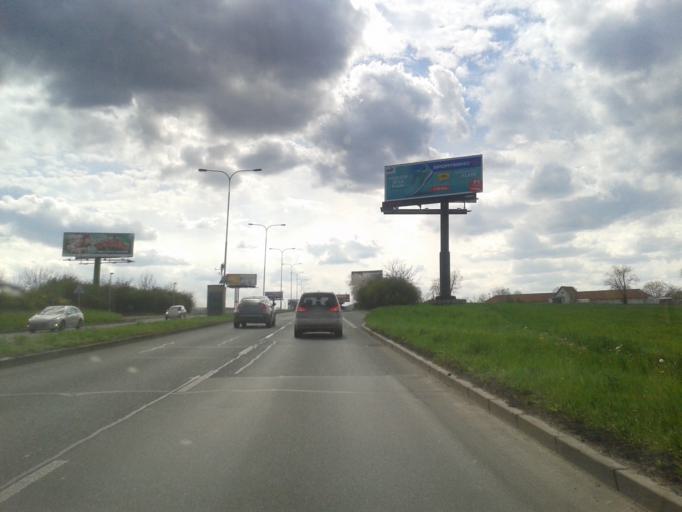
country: CZ
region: Praha
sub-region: Praha 12
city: Modrany
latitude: 50.0239
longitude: 14.3542
